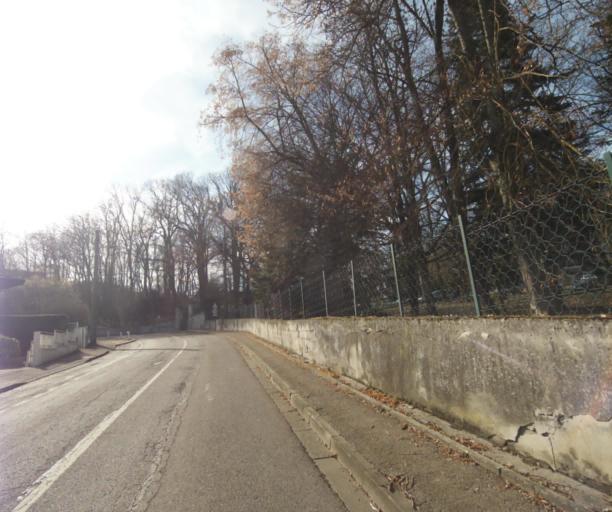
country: FR
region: Lorraine
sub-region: Departement de Meurthe-et-Moselle
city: Villers-les-Nancy
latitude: 48.6746
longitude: 6.1452
